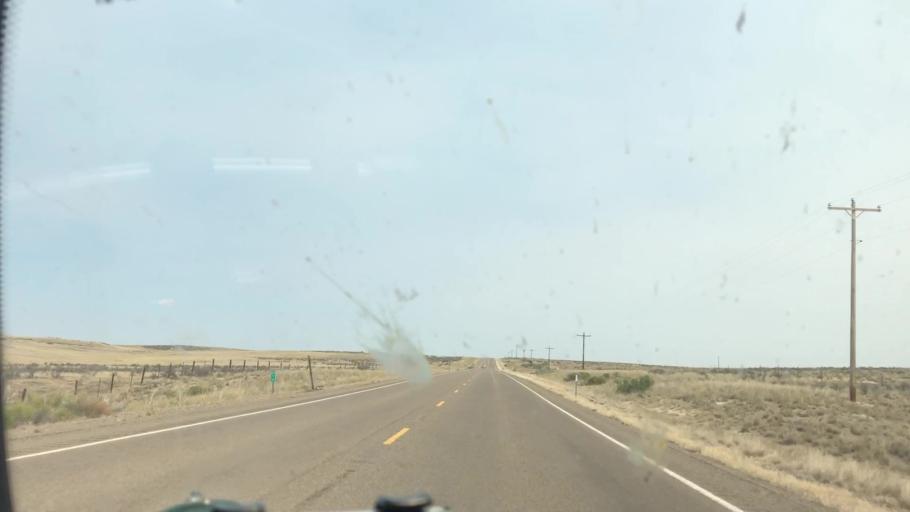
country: US
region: Idaho
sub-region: Owyhee County
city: Homedale
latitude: 42.8558
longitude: -117.5780
